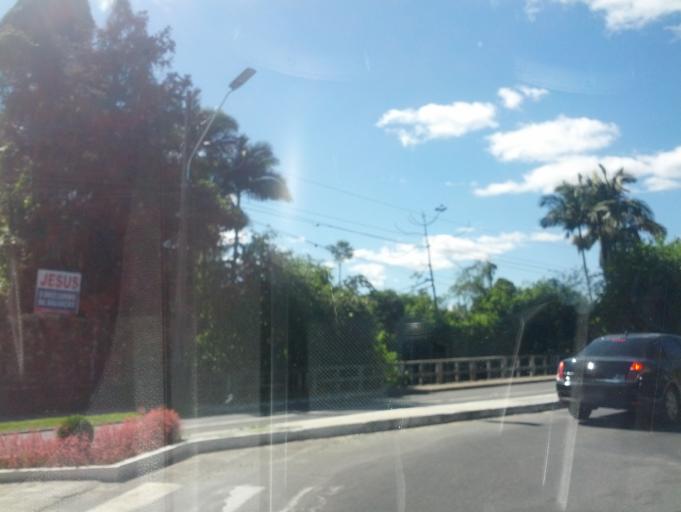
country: BR
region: Santa Catarina
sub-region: Blumenau
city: Blumenau
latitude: -26.9104
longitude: -49.0818
